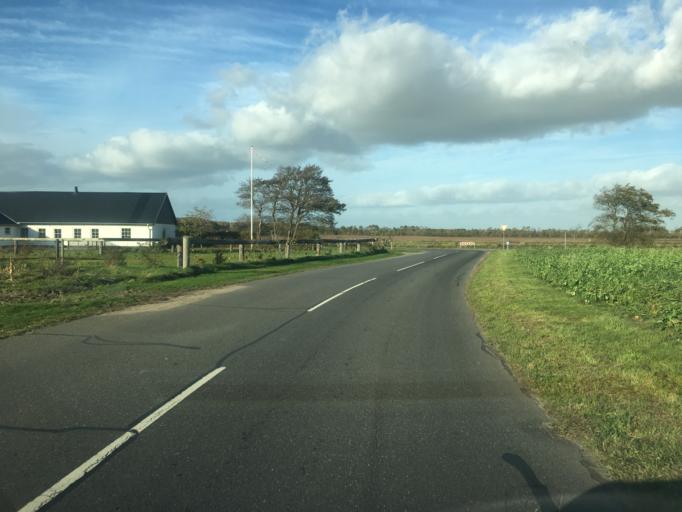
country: DK
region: South Denmark
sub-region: Tonder Kommune
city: Logumkloster
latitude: 55.0727
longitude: 8.9430
